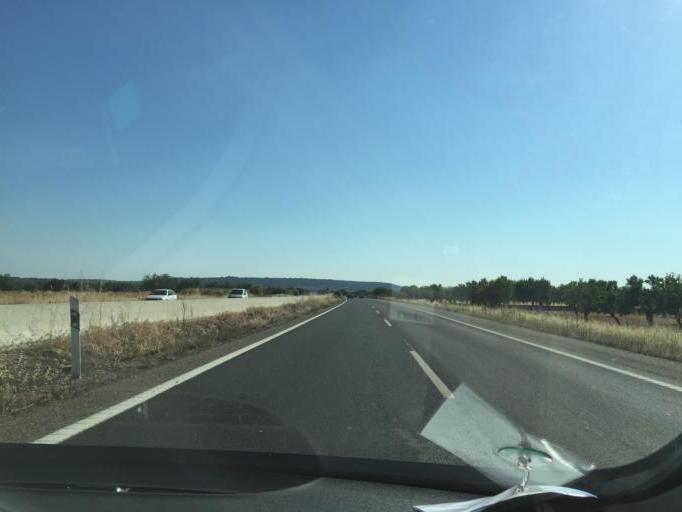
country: ES
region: Balearic Islands
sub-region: Illes Balears
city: Consell
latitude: 39.6616
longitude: 2.8107
